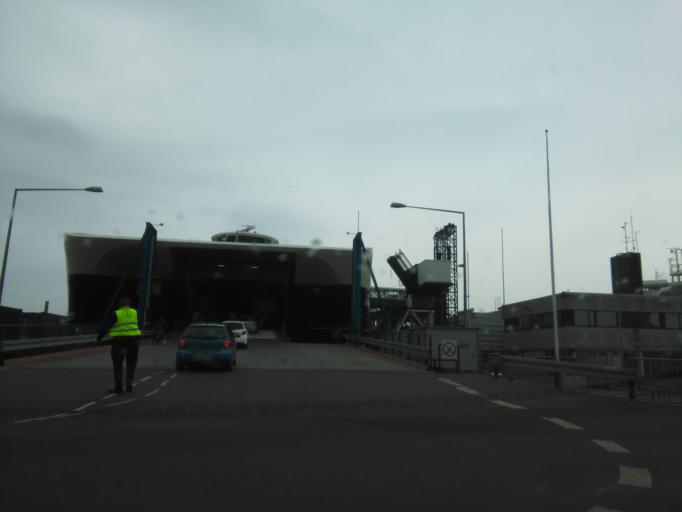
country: DK
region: Capital Region
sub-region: Bornholm Kommune
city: Ronne
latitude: 55.1001
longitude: 14.6913
